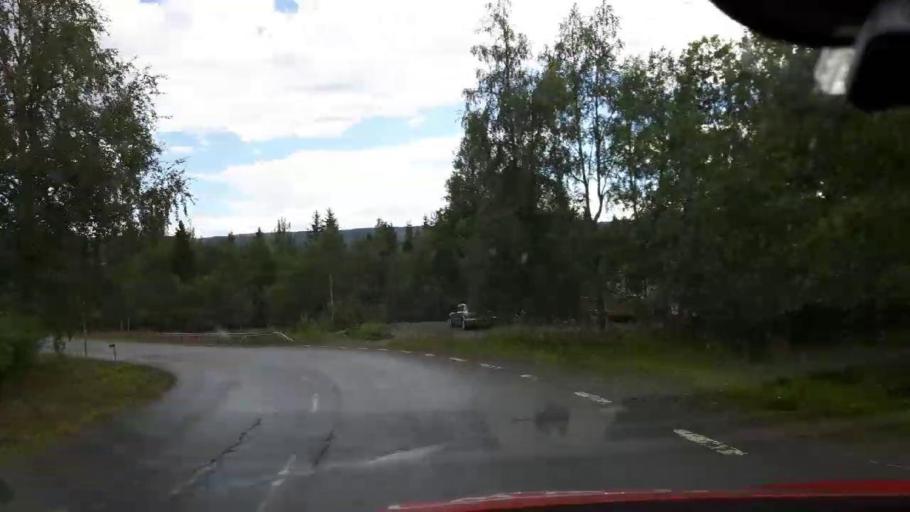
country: SE
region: Jaemtland
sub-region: Are Kommun
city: Are
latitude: 63.3186
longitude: 13.2309
